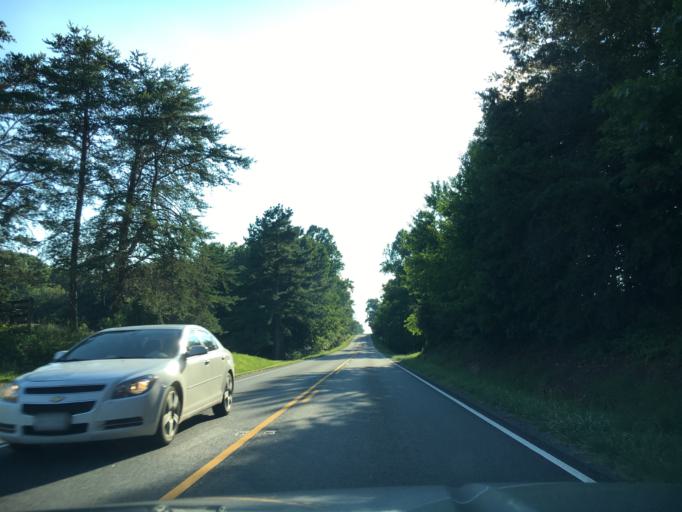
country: US
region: Virginia
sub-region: City of Bedford
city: Bedford
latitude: 37.2407
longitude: -79.6125
